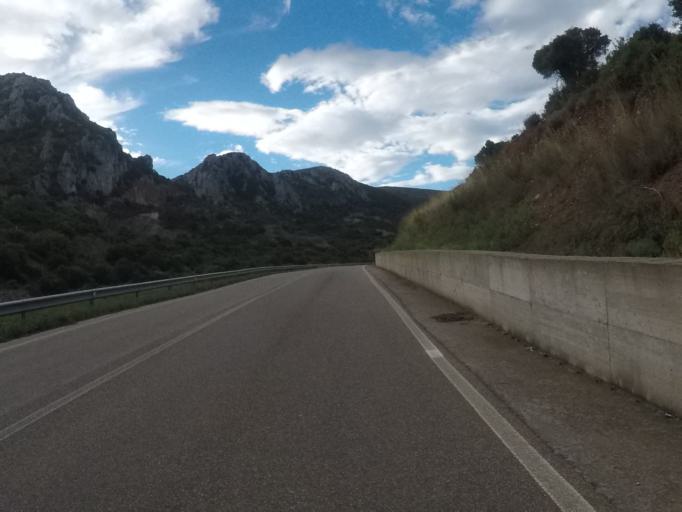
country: IT
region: Sardinia
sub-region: Provincia di Carbonia-Iglesias
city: Buggerru
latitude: 39.3614
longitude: 8.4401
